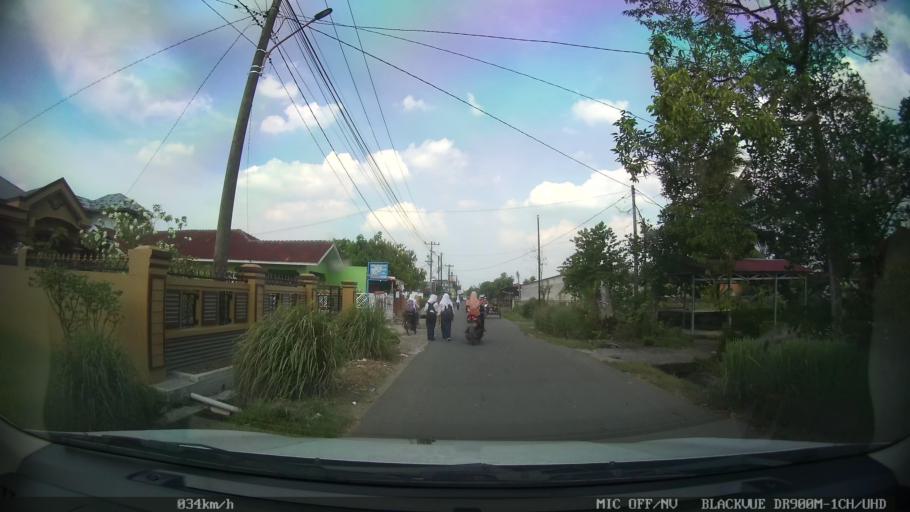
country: ID
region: North Sumatra
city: Binjai
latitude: 3.6133
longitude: 98.5276
